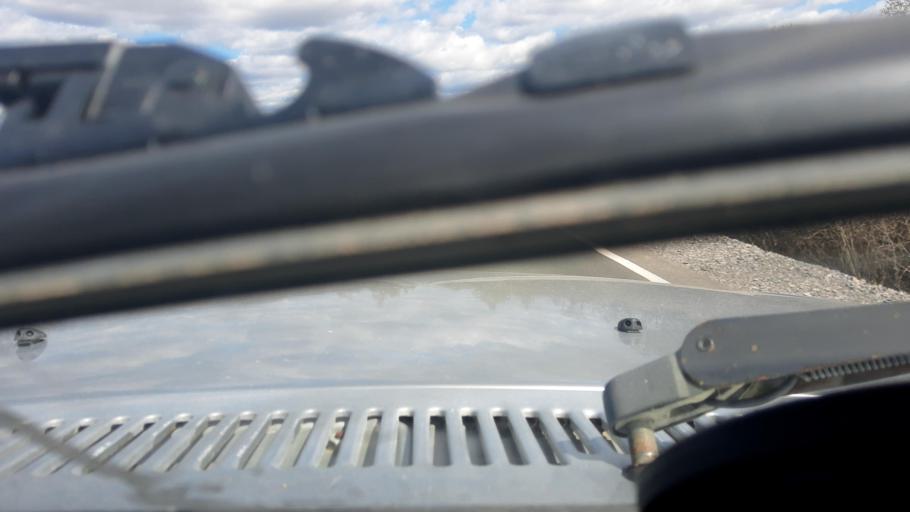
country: RU
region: Bashkortostan
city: Yazykovo
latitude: 55.2999
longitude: 56.3034
